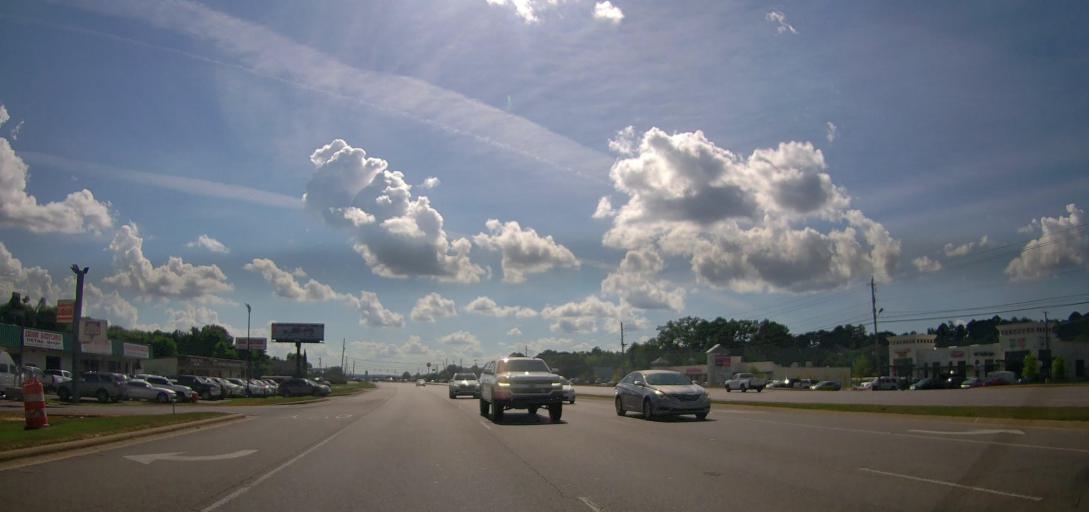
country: US
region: Alabama
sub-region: Tuscaloosa County
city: Northport
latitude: 33.2406
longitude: -87.5886
